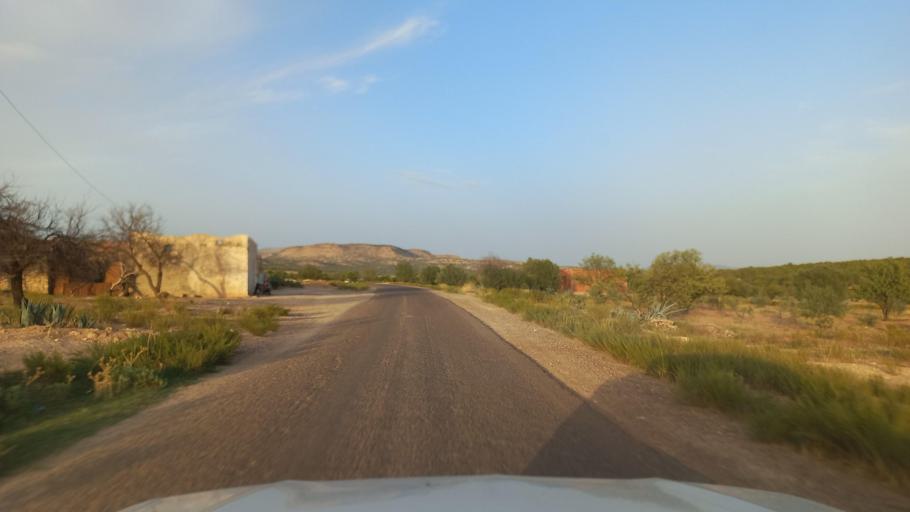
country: TN
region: Al Qasrayn
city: Sbiba
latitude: 35.4083
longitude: 8.9136
